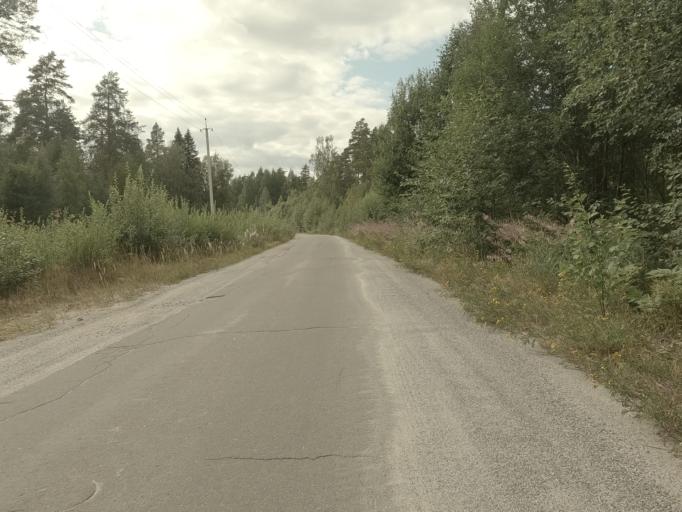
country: RU
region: Leningrad
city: Kamennogorsk
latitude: 60.9708
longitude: 29.1546
